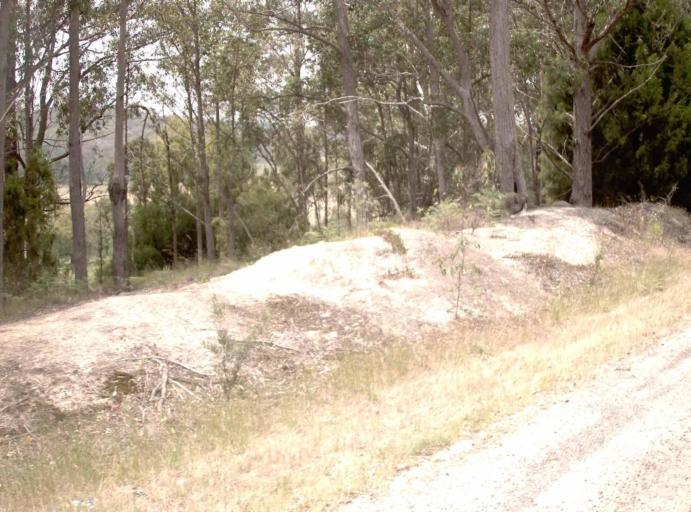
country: AU
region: Victoria
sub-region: Latrobe
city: Traralgon
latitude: -38.4442
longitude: 146.7338
